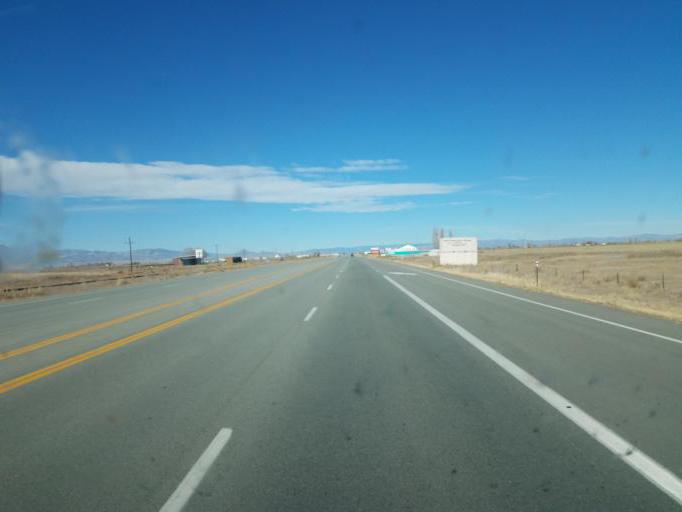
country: US
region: Colorado
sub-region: Rio Grande County
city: Monte Vista
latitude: 37.5296
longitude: -106.0228
